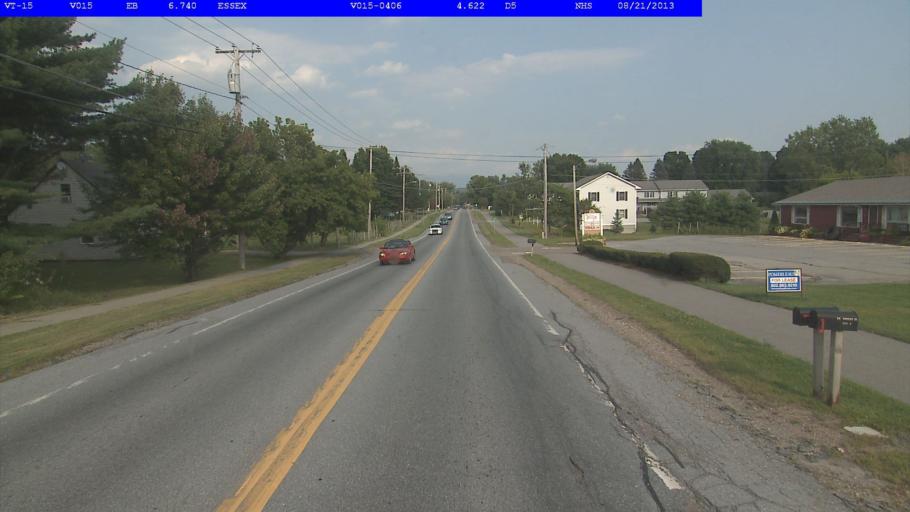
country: US
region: Vermont
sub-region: Chittenden County
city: Essex Junction
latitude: 44.5104
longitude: -73.0742
